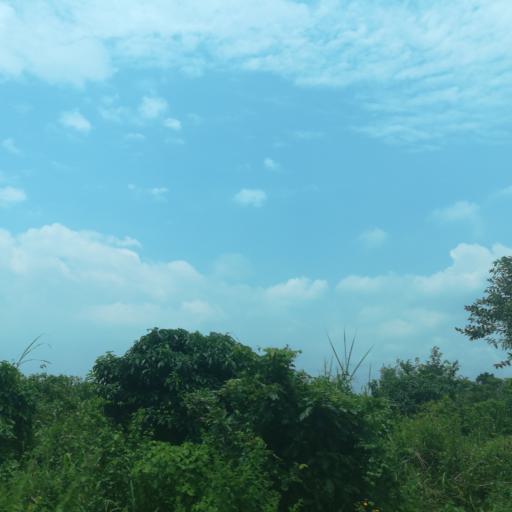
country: NG
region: Lagos
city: Ejirin
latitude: 6.6603
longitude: 3.8071
